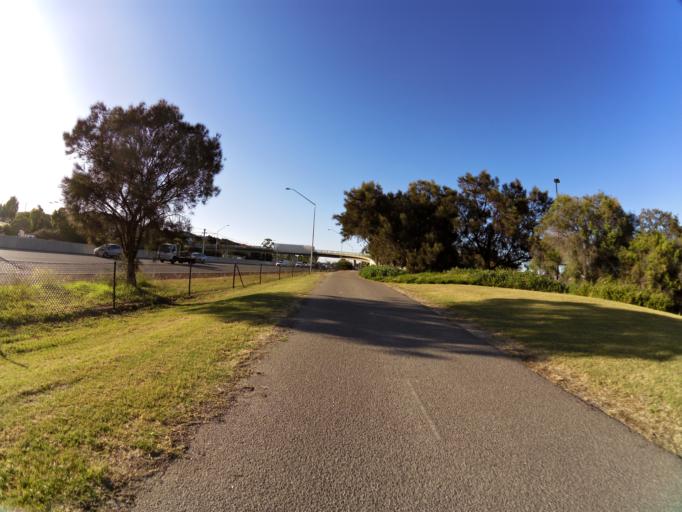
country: AU
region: Western Australia
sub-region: South Perth
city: Manning
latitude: -32.0164
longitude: 115.8572
